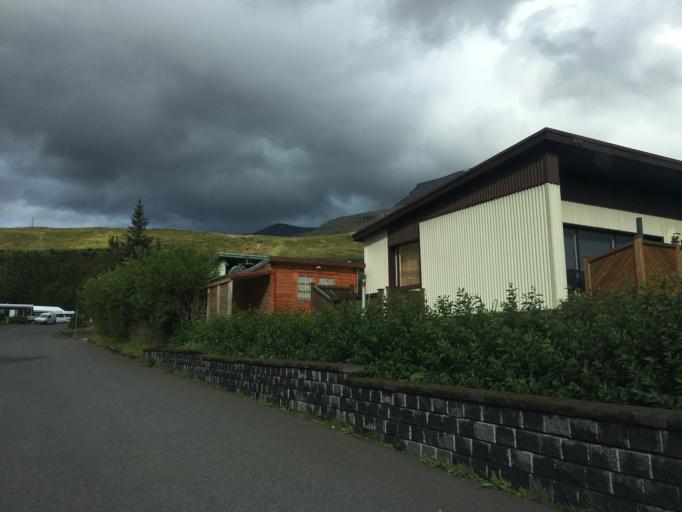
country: IS
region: East
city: Reydarfjoerdur
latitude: 65.0359
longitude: -14.2141
